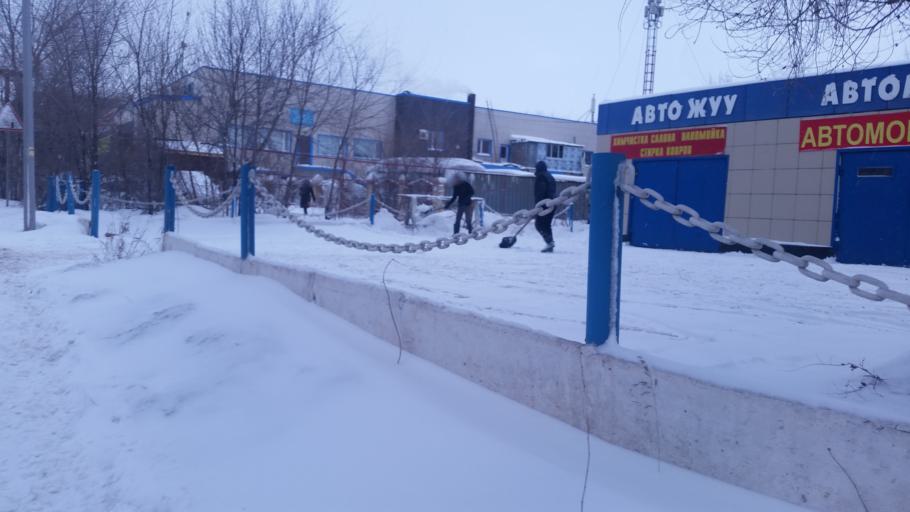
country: KZ
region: Qaraghandy
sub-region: Qaraghandy Qalasy
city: Karagandy
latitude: 49.7691
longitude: 73.1490
